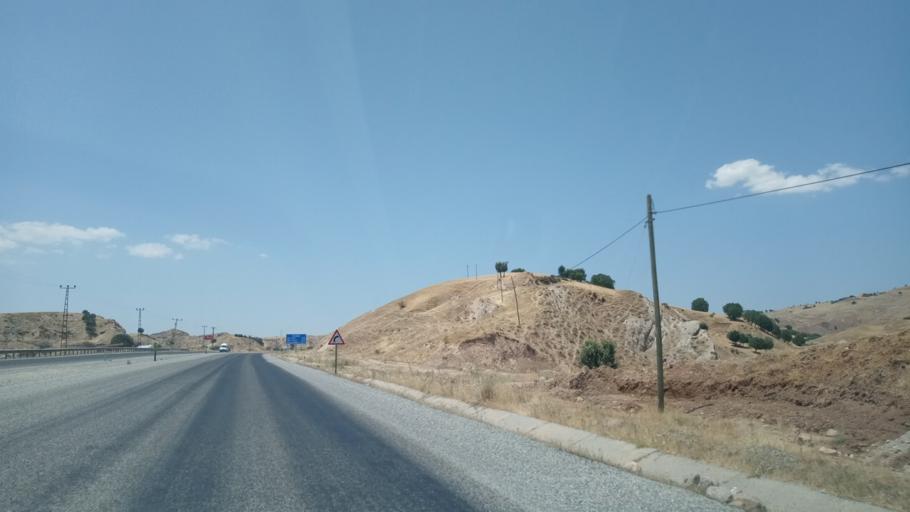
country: TR
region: Batman
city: Kozluk
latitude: 38.1679
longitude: 41.4755
